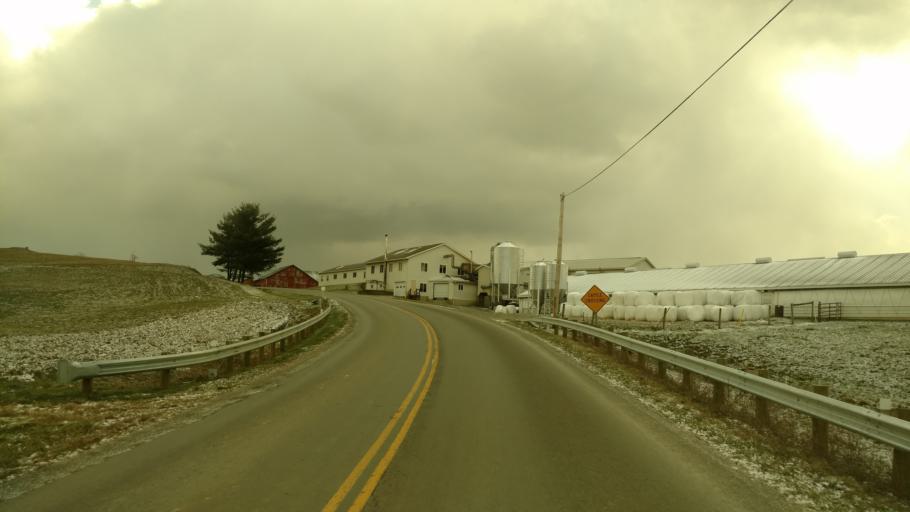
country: US
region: Ohio
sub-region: Holmes County
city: Millersburg
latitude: 40.4862
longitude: -81.7885
